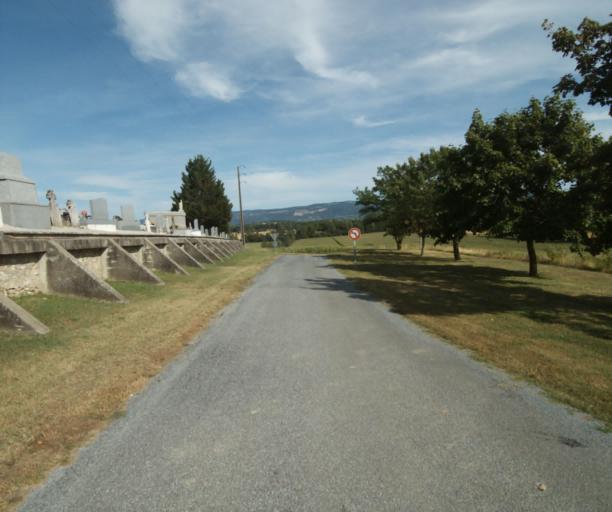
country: FR
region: Midi-Pyrenees
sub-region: Departement du Tarn
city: Puylaurens
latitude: 43.5241
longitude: 2.0559
